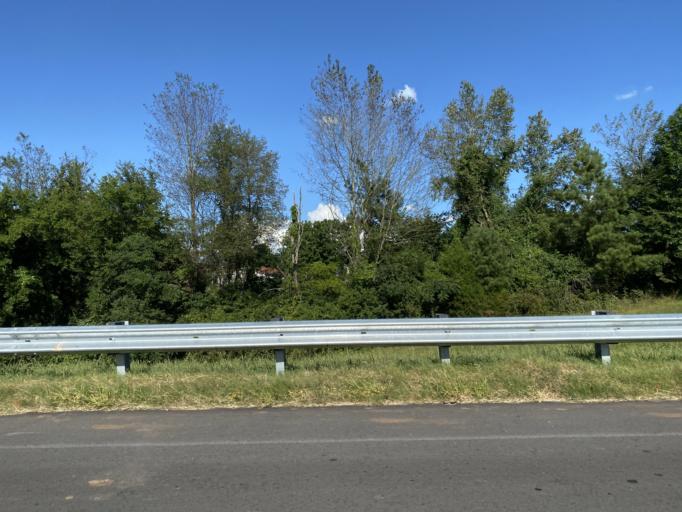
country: US
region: Alabama
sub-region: Limestone County
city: Athens
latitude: 34.7552
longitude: -86.9381
